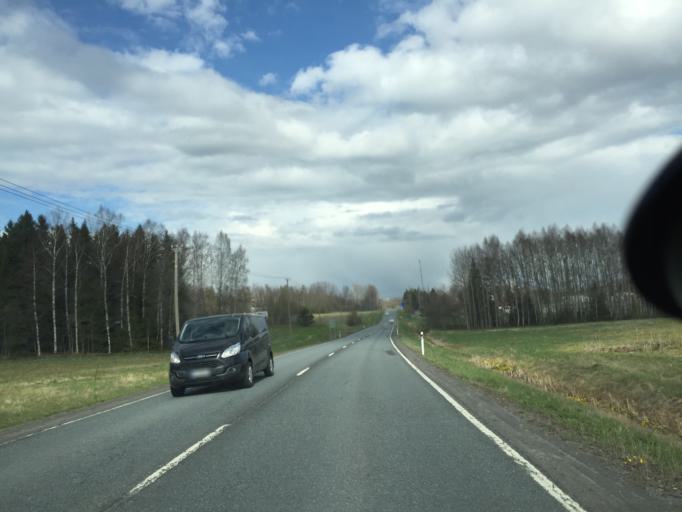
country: FI
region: Uusimaa
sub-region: Helsinki
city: Lohja
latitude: 60.1746
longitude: 23.9743
